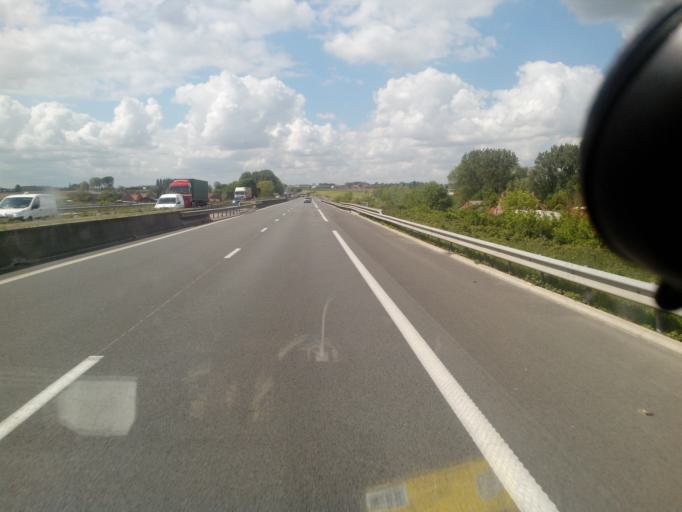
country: FR
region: Nord-Pas-de-Calais
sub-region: Departement du Nord
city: Meteren
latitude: 50.7419
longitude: 2.6806
